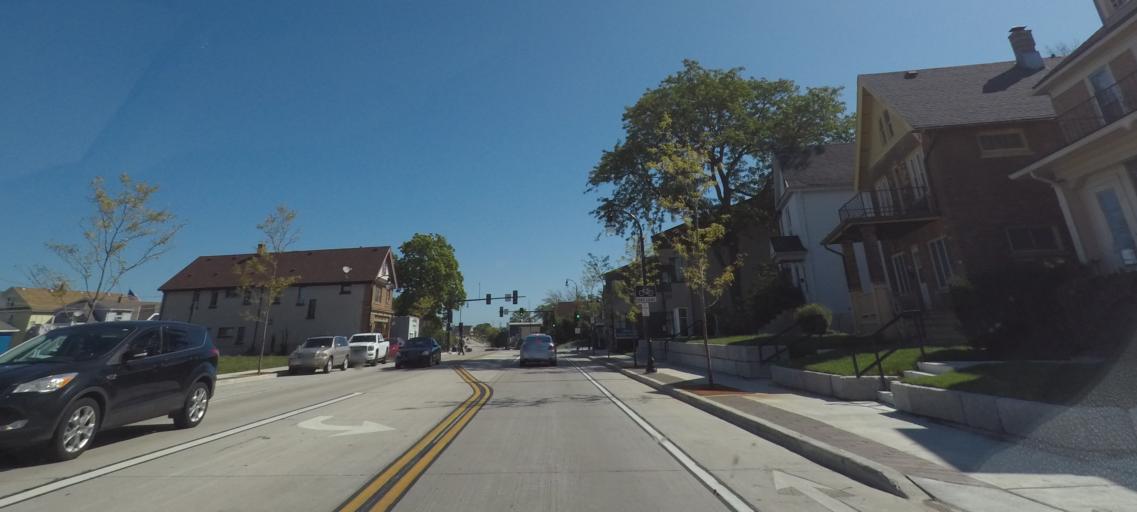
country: US
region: Wisconsin
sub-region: Milwaukee County
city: West Allis
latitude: 43.0128
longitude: -88.0012
